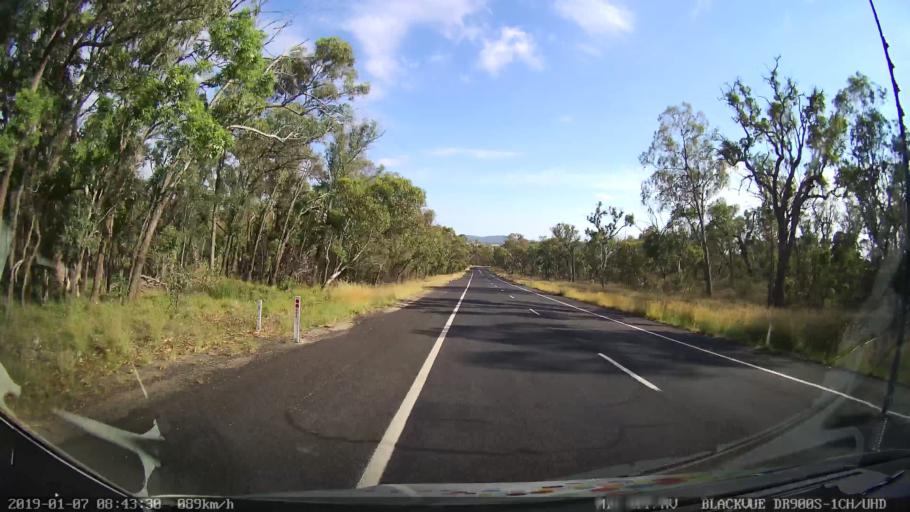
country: AU
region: New South Wales
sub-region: Tamworth Municipality
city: Kootingal
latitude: -30.8440
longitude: 151.2152
